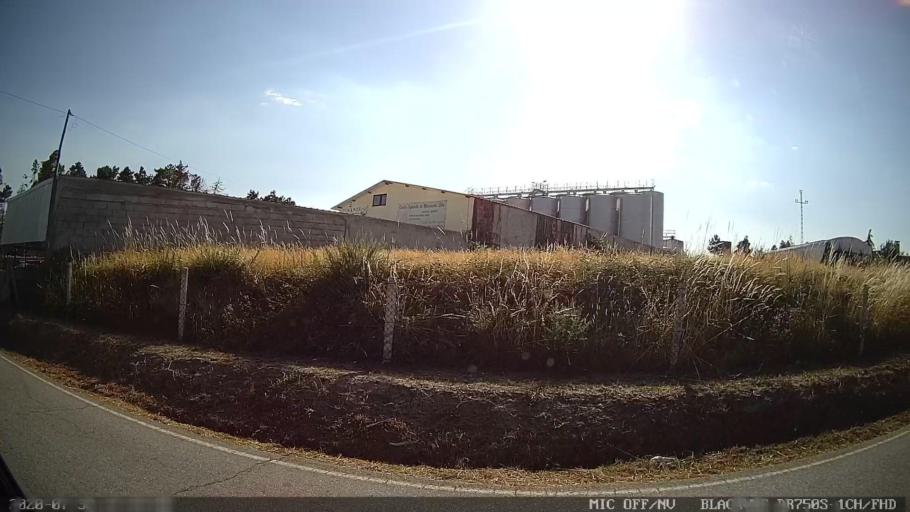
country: PT
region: Vila Real
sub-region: Murca
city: Murca
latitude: 41.3823
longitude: -7.5005
